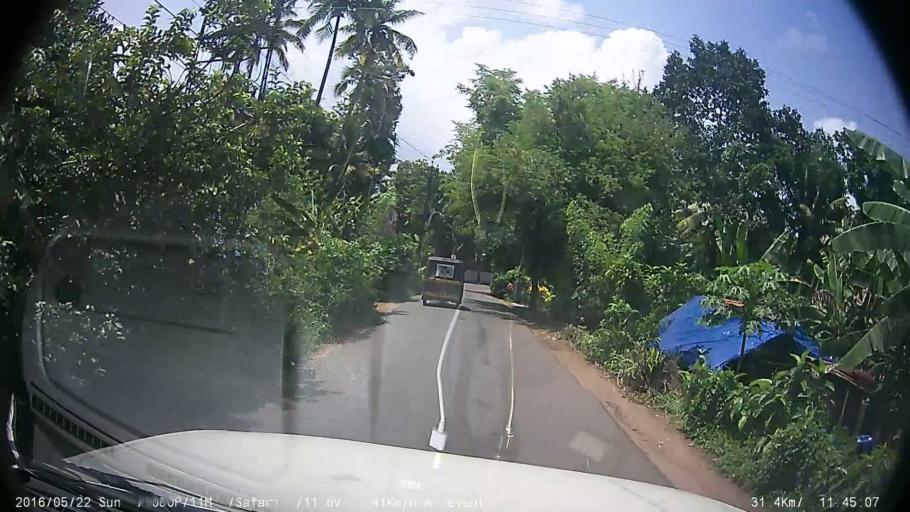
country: IN
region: Kerala
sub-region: Kottayam
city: Kottayam
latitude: 9.5410
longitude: 76.5204
